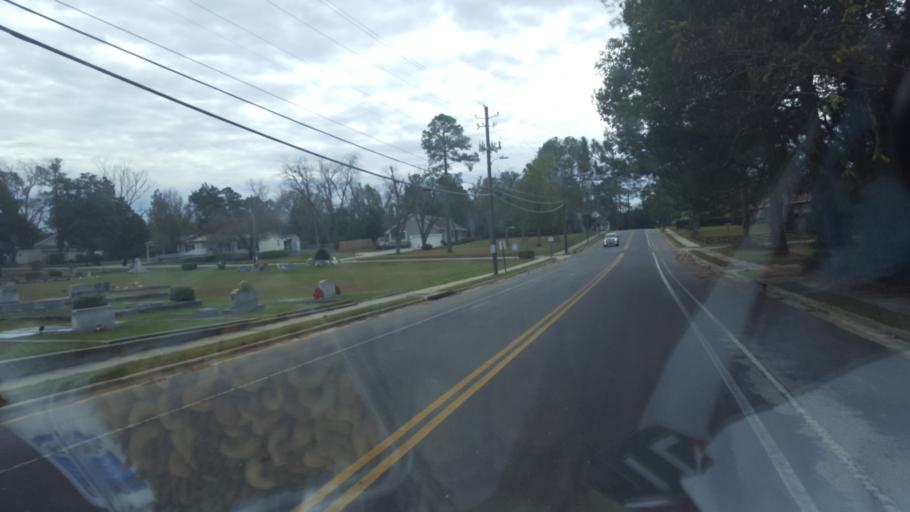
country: US
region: Georgia
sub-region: Berrien County
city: Nashville
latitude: 31.2059
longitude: -83.2547
